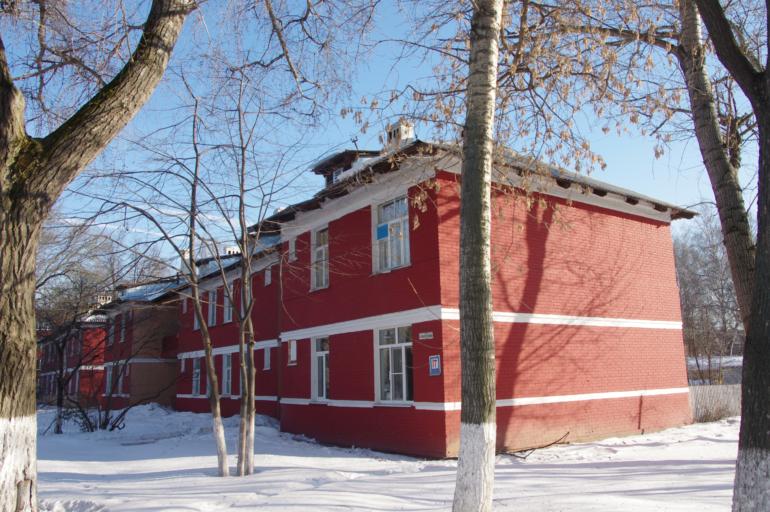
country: RU
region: Moskovskaya
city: Kolomna
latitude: 55.0929
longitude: 38.7717
